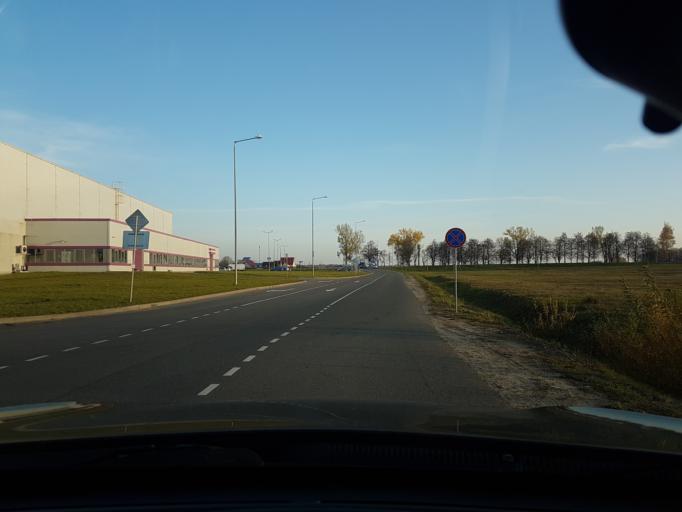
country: BY
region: Minsk
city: Shchomyslitsa
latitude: 53.8222
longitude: 27.4338
